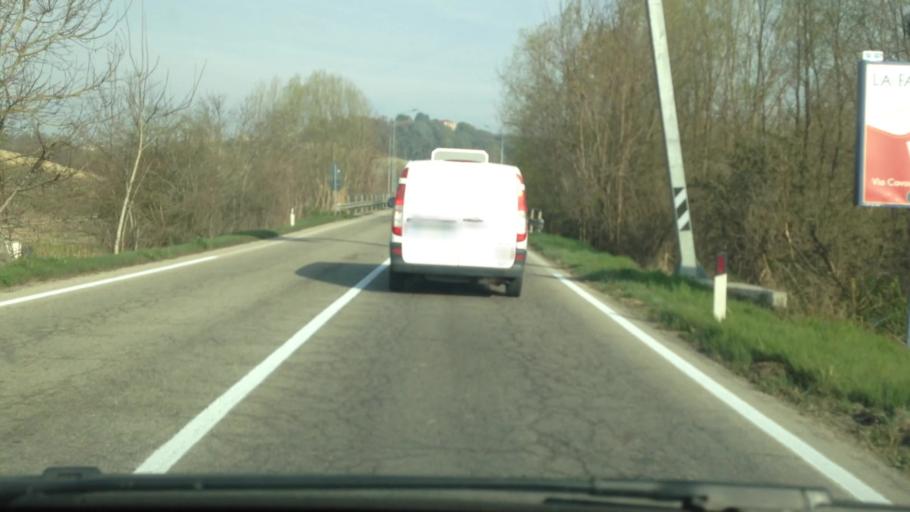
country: IT
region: Piedmont
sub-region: Provincia di Cuneo
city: Canale
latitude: 44.8010
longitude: 7.9794
